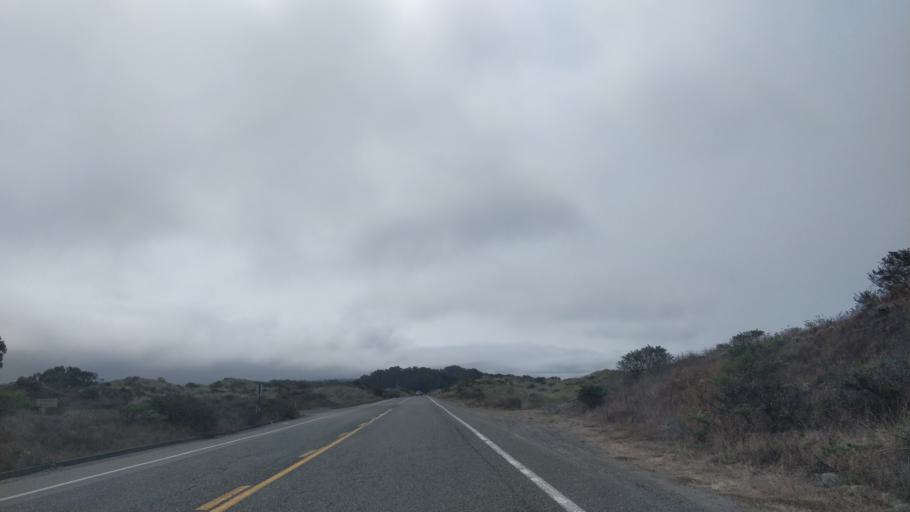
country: US
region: California
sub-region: Humboldt County
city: Bayview
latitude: 40.7888
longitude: -124.2068
